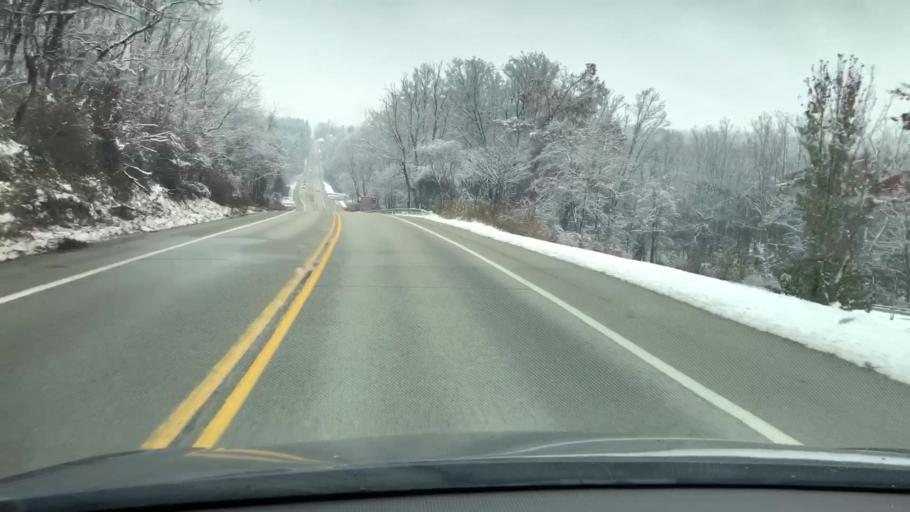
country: US
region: Pennsylvania
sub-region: Fayette County
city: Hopwood
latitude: 39.8177
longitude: -79.5869
